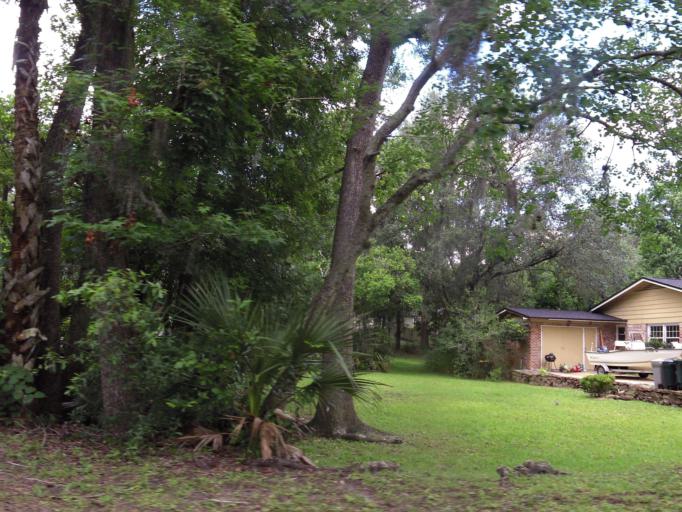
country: US
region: Florida
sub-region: Duval County
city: Jacksonville
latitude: 30.2960
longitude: -81.6437
